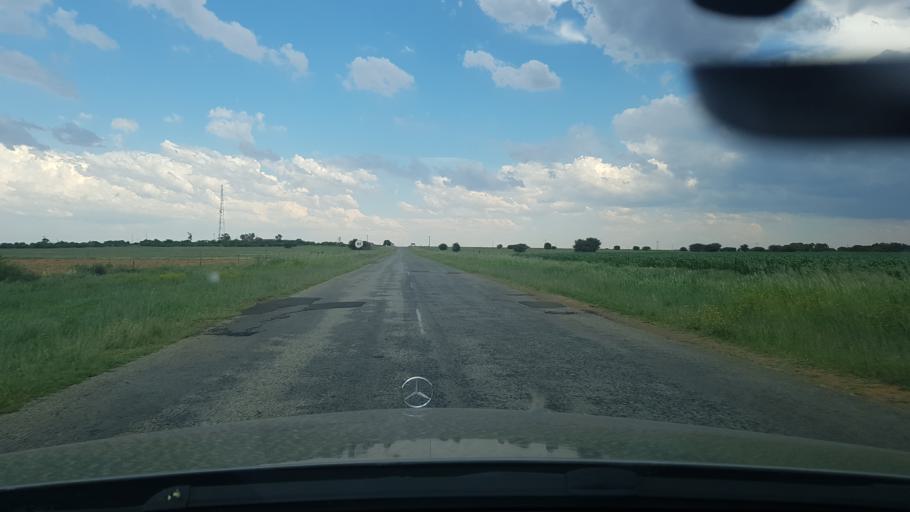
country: ZA
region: Orange Free State
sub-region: Lejweleputswa District Municipality
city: Hoopstad
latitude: -27.9496
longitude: 25.7008
